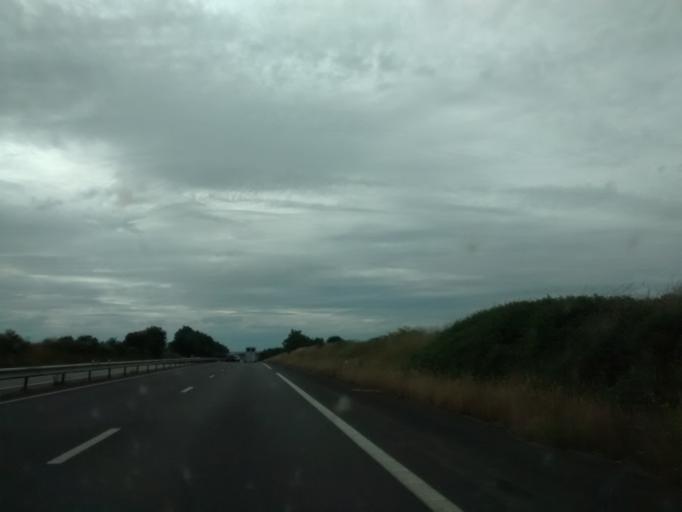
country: FR
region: Brittany
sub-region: Departement des Cotes-d'Armor
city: Caulnes
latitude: 48.2844
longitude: -2.1978
